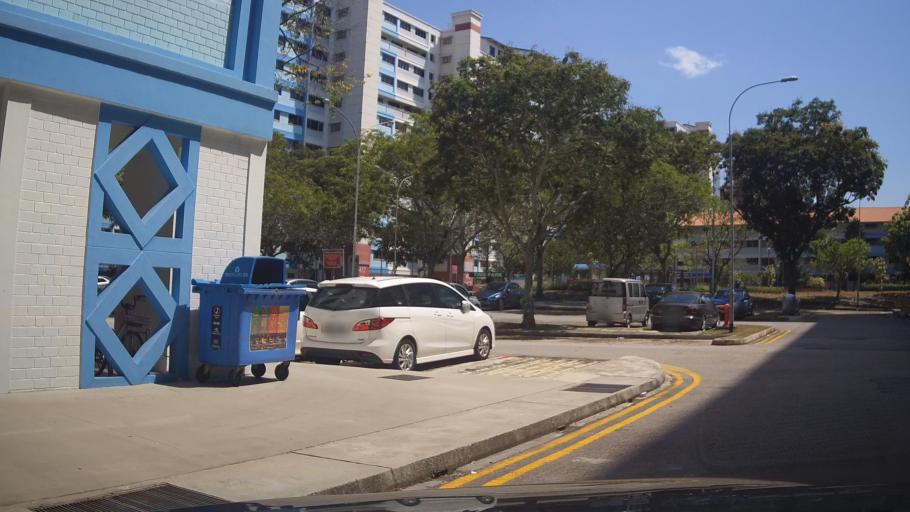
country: MY
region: Johor
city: Kampung Pasir Gudang Baru
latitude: 1.3725
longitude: 103.9544
